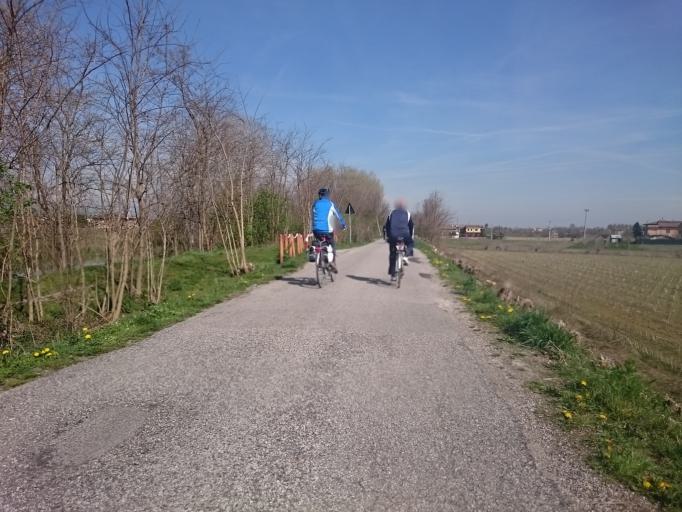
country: IT
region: Veneto
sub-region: Provincia di Padova
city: Sarmeola
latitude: 45.4217
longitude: 11.8285
